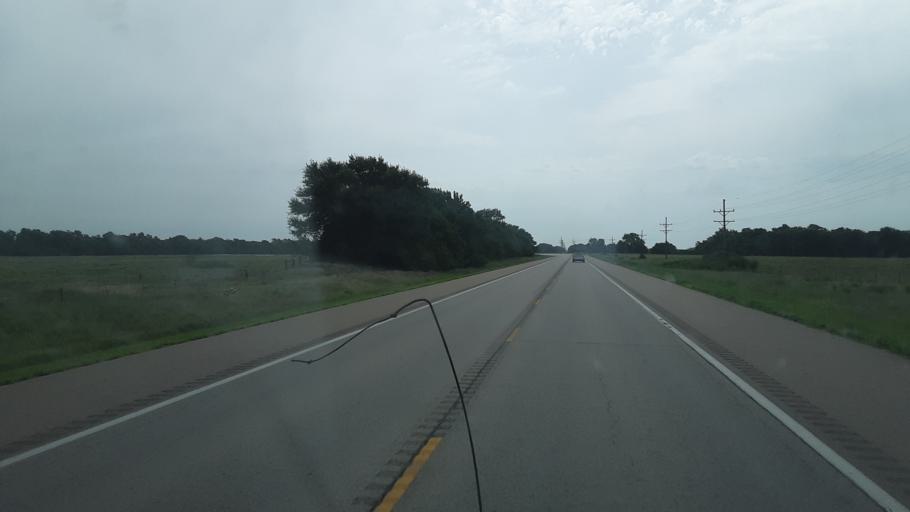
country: US
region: Kansas
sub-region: Stafford County
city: Stafford
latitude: 37.9552
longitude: -98.4314
